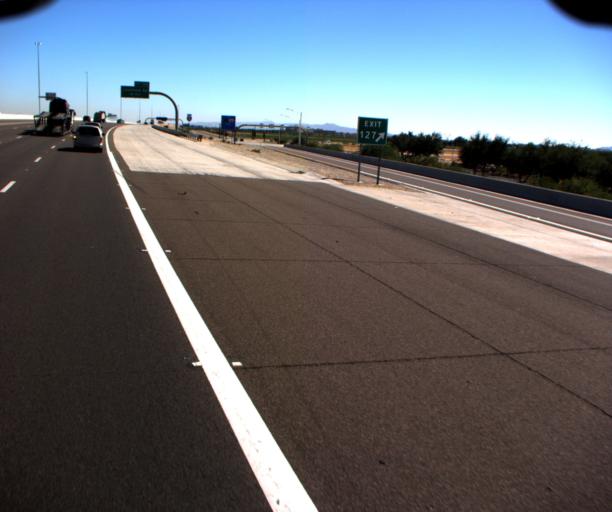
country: US
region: Arizona
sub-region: Maricopa County
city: Goodyear
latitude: 33.4609
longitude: -112.3790
